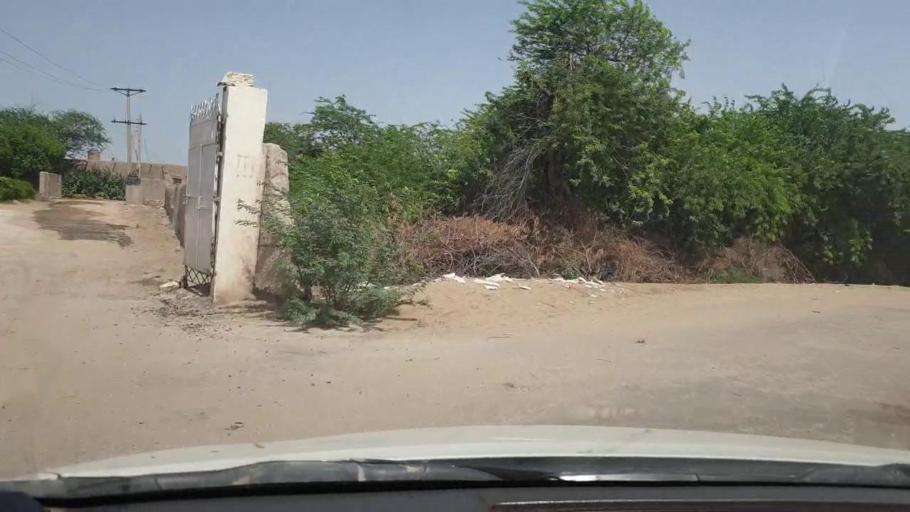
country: PK
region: Sindh
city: Rohri
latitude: 27.5023
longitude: 69.0414
